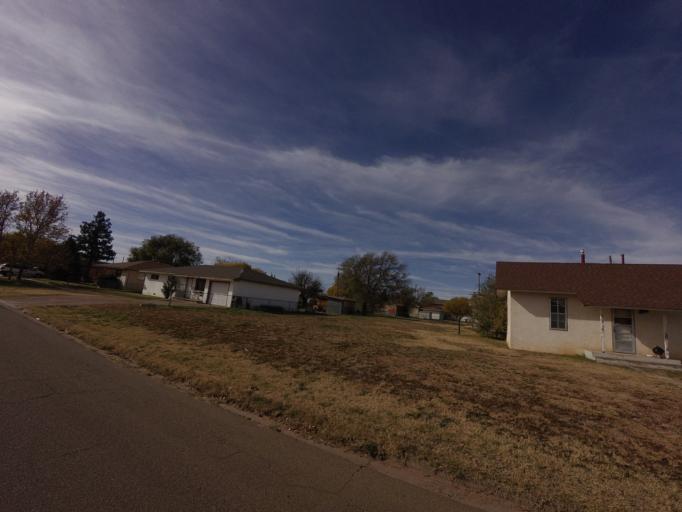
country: US
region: New Mexico
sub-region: Curry County
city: Clovis
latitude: 34.4118
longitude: -103.1890
